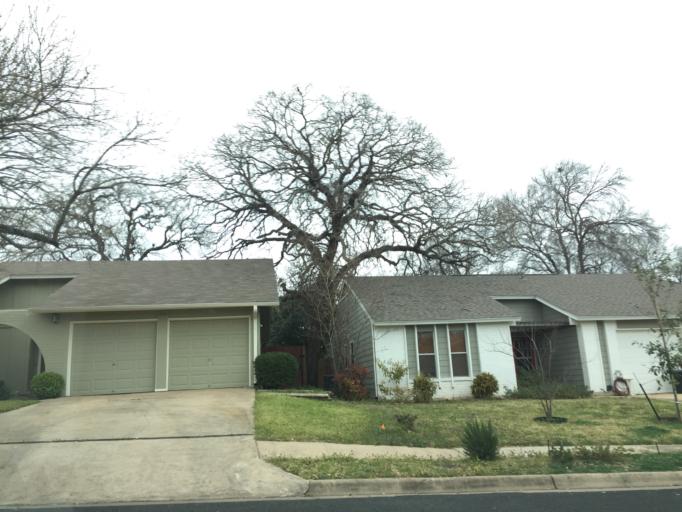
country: US
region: Texas
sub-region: Williamson County
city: Jollyville
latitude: 30.4154
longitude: -97.7413
